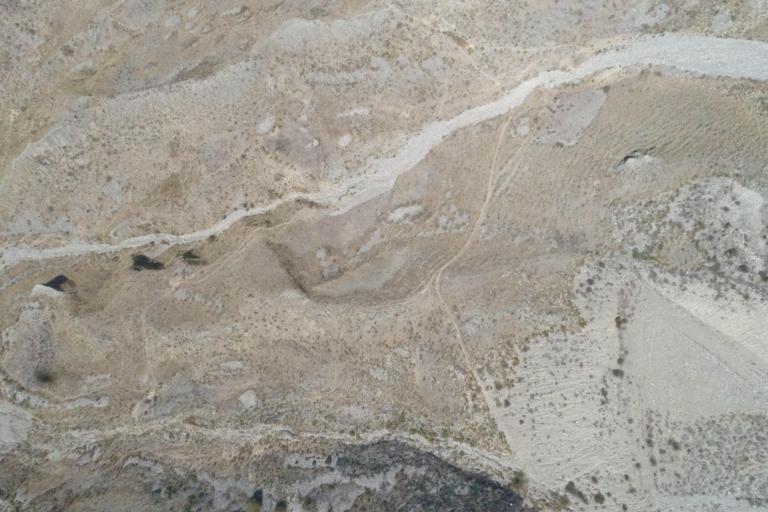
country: BO
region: La Paz
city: La Paz
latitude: -16.4724
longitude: -68.0956
